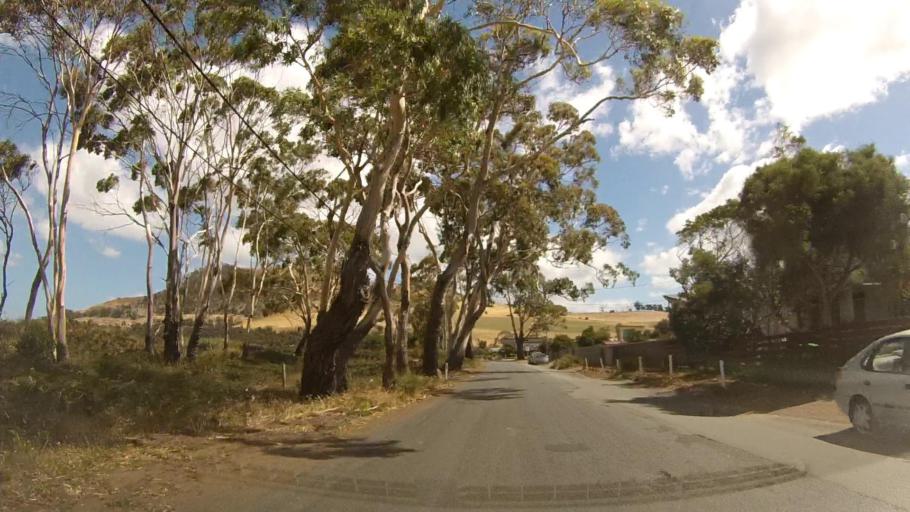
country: AU
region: Tasmania
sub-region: Clarence
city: Seven Mile Beach
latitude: -42.8625
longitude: 147.5049
